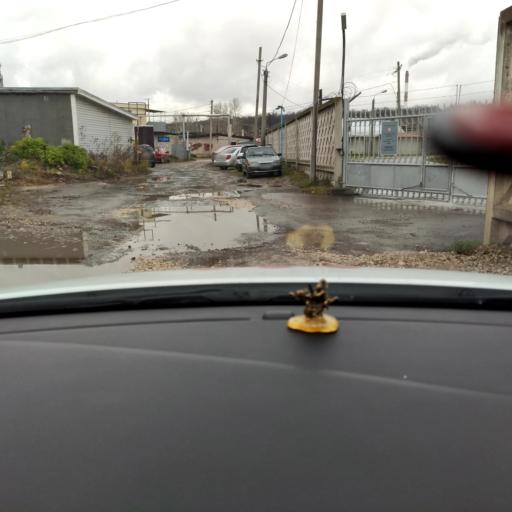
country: RU
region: Tatarstan
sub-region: Gorod Kazan'
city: Kazan
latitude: 55.7586
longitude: 49.2071
